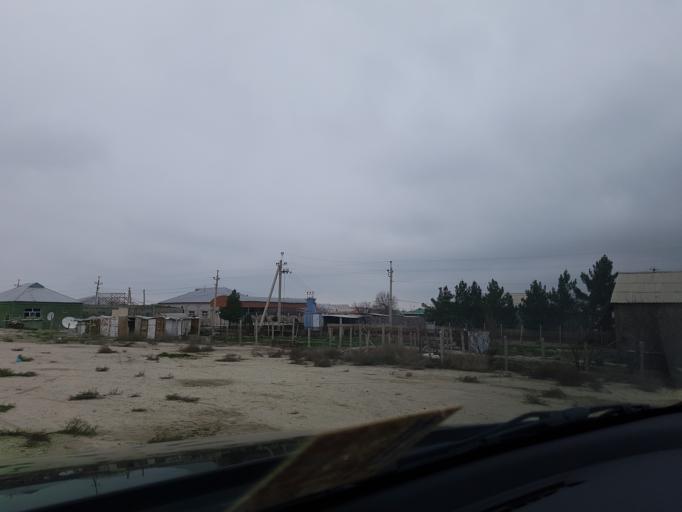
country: TM
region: Ahal
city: Abadan
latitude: 38.1418
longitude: 57.9672
